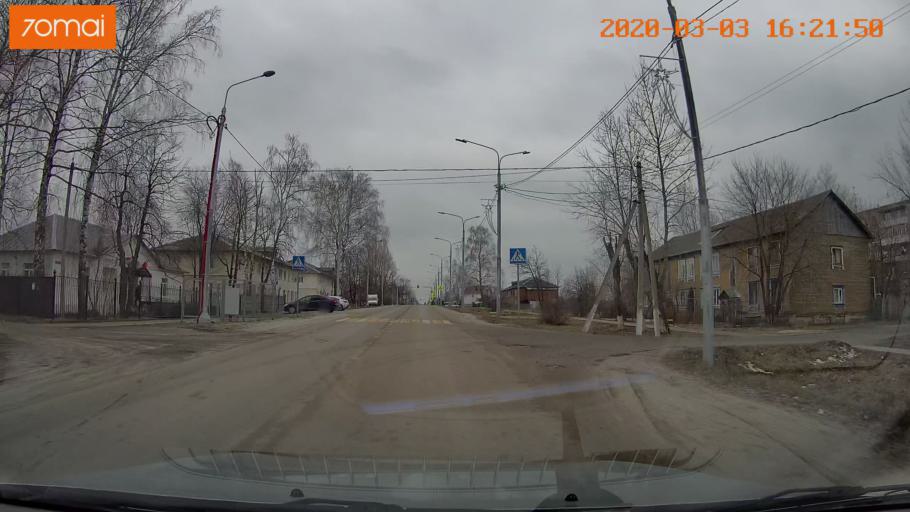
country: RU
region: Moskovskaya
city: Imeni Tsyurupy
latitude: 55.4953
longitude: 38.6461
